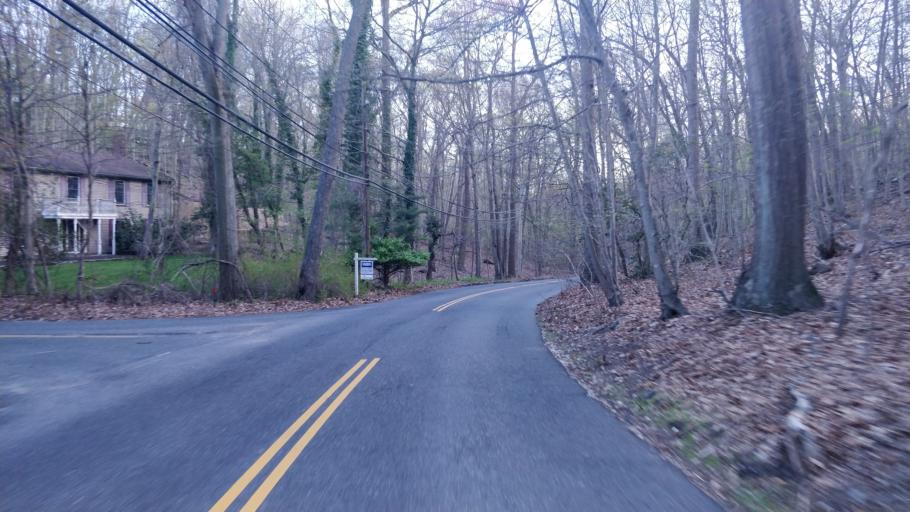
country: US
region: New York
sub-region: Suffolk County
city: Village of the Branch
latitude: 40.8811
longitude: -73.1850
